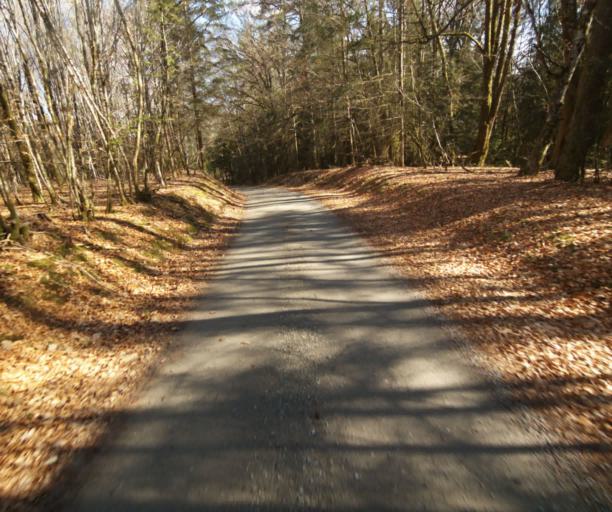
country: FR
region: Limousin
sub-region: Departement de la Correze
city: Correze
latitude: 45.2547
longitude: 1.9220
